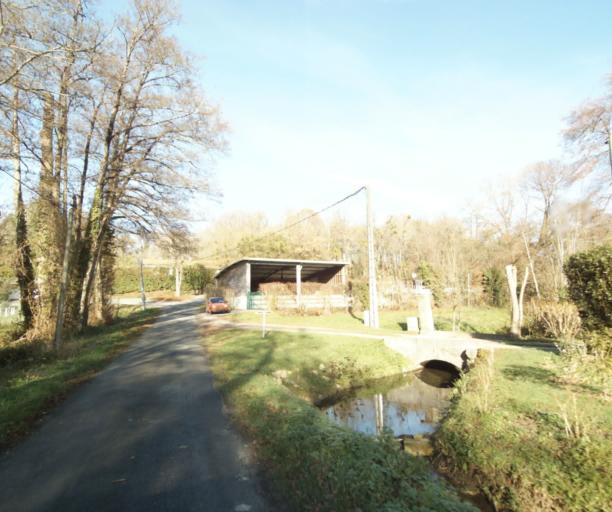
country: FR
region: Poitou-Charentes
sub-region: Departement de la Charente-Maritime
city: Ecoyeux
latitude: 45.7624
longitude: -0.4973
